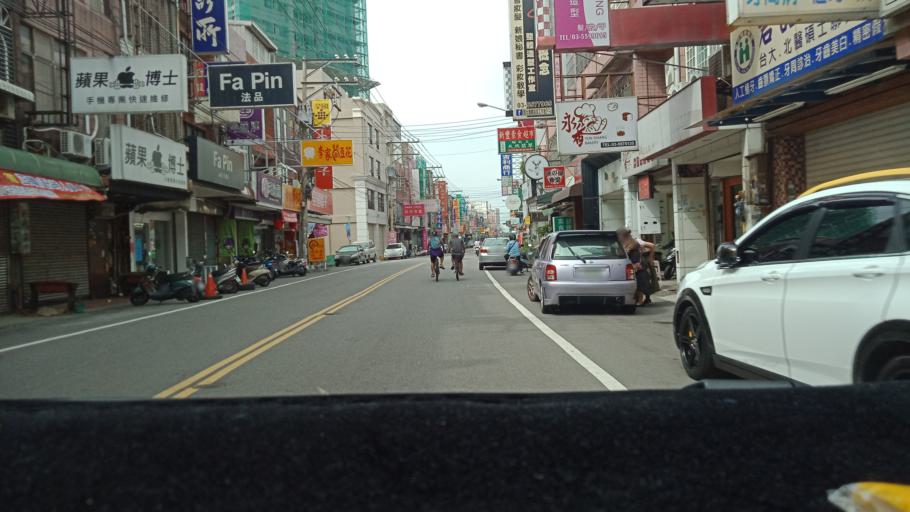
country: TW
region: Taiwan
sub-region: Hsinchu
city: Zhubei
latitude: 24.8713
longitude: 120.9954
